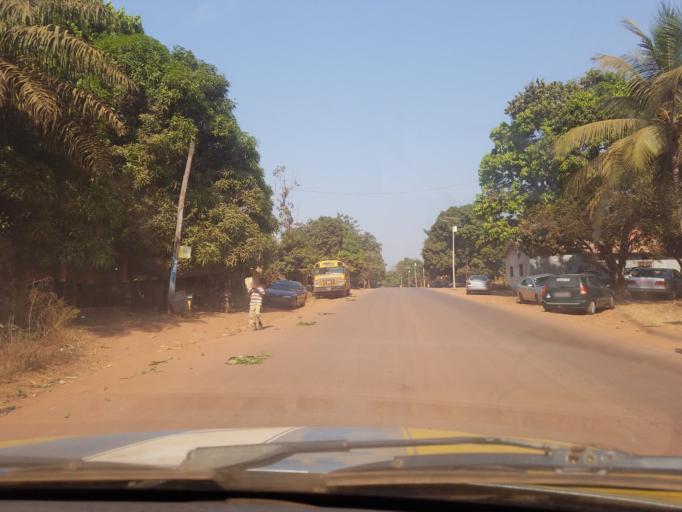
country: GN
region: Boke
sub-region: Boke Prefecture
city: Sangueya
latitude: 10.8055
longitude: -14.3887
